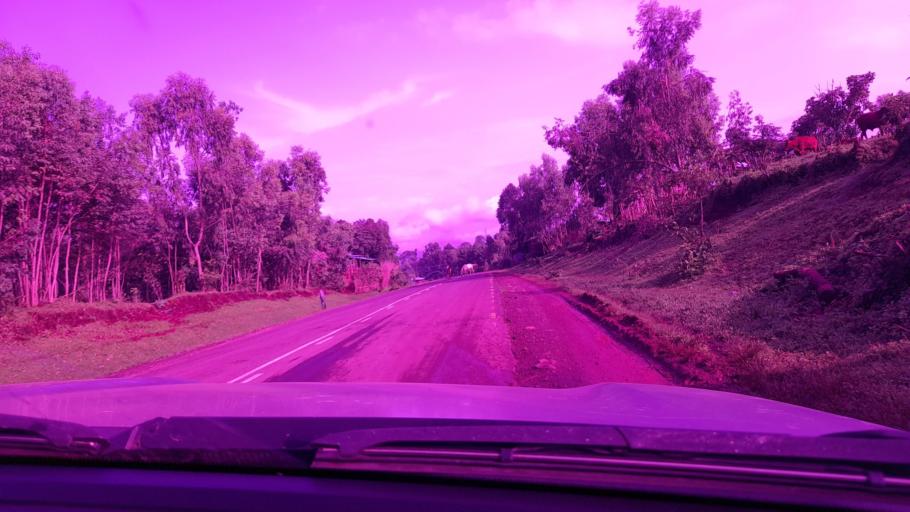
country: ET
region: Oromiya
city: Bedele
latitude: 8.1885
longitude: 36.4470
